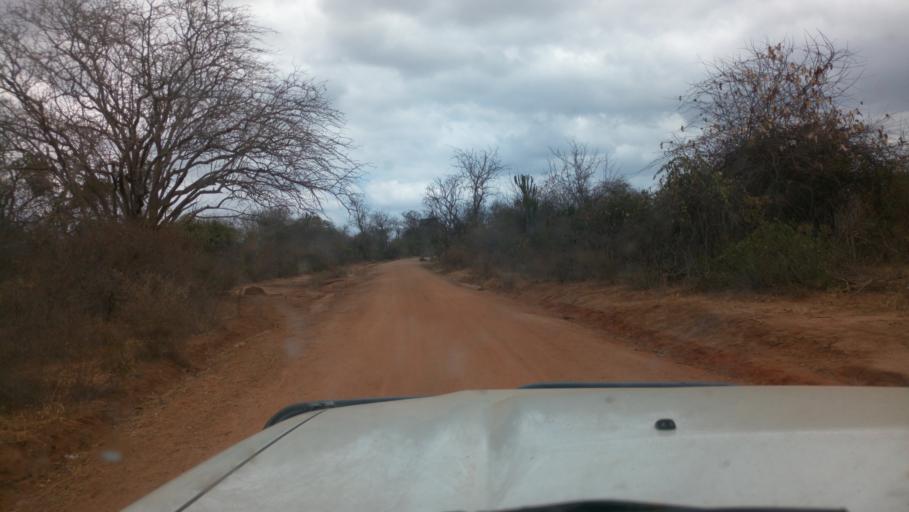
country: KE
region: Kitui
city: Kitui
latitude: -1.8994
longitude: 38.4196
